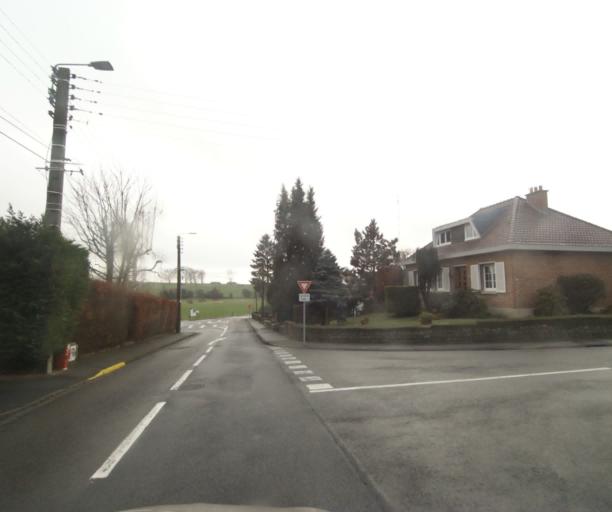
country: FR
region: Nord-Pas-de-Calais
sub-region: Departement du Nord
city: Aulnoy-lez-Valenciennes
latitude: 50.3266
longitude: 3.5257
